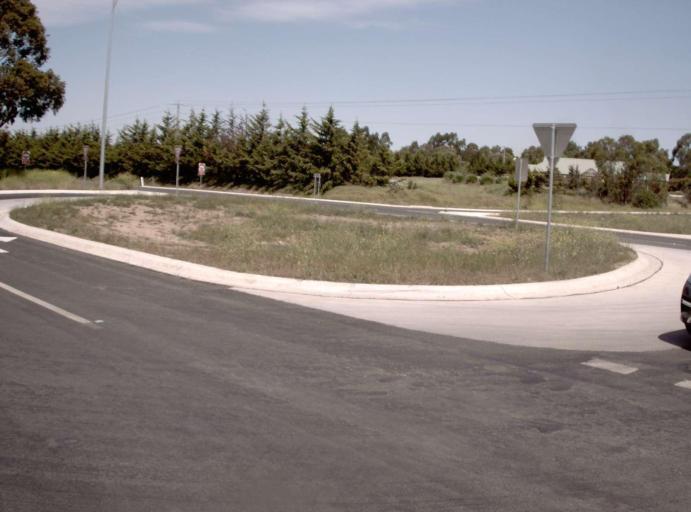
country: AU
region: Victoria
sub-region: Wellington
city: Sale
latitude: -38.1033
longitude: 147.0218
